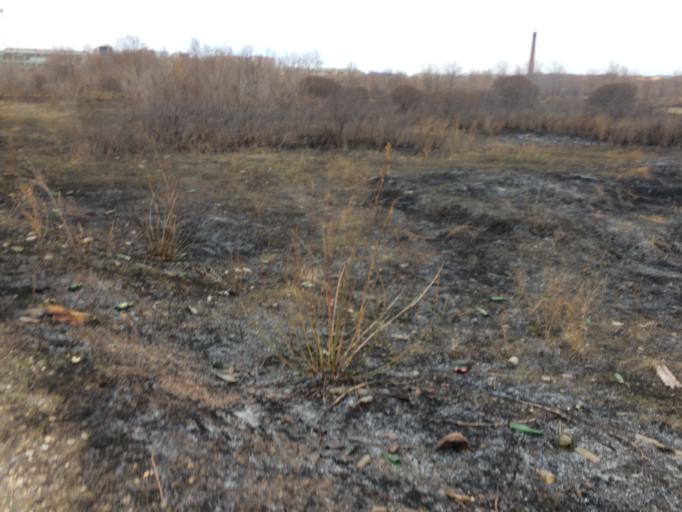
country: RU
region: Chelyabinsk
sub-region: Gorod Magnitogorsk
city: Magnitogorsk
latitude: 53.4419
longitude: 58.9764
